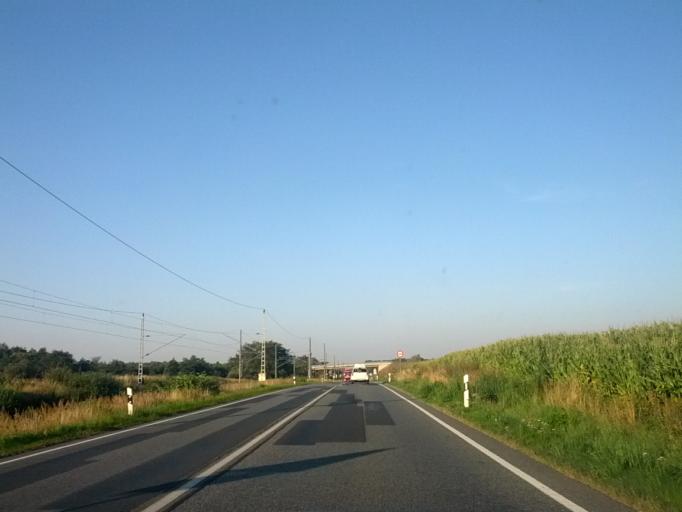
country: DE
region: Mecklenburg-Vorpommern
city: Samtens
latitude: 54.3653
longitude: 13.3168
